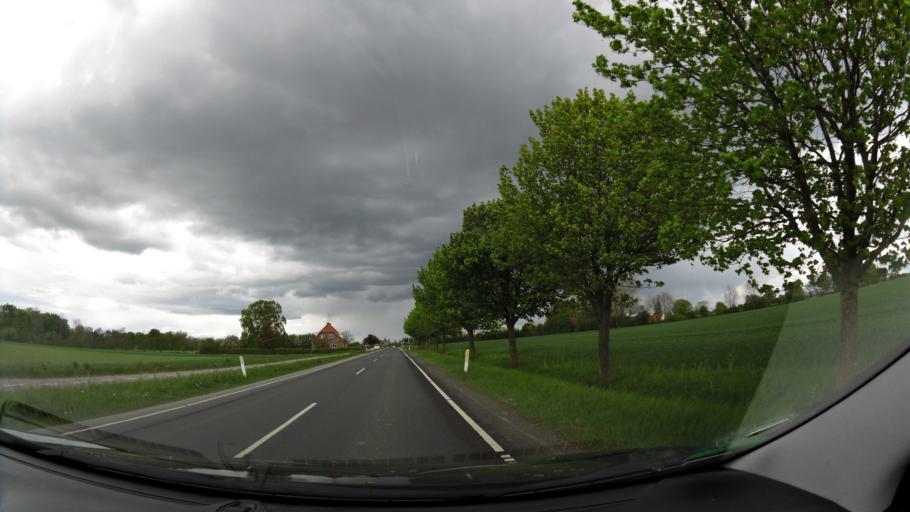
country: DK
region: South Denmark
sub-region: Nyborg Kommune
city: Nyborg
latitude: 55.2151
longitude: 10.7313
